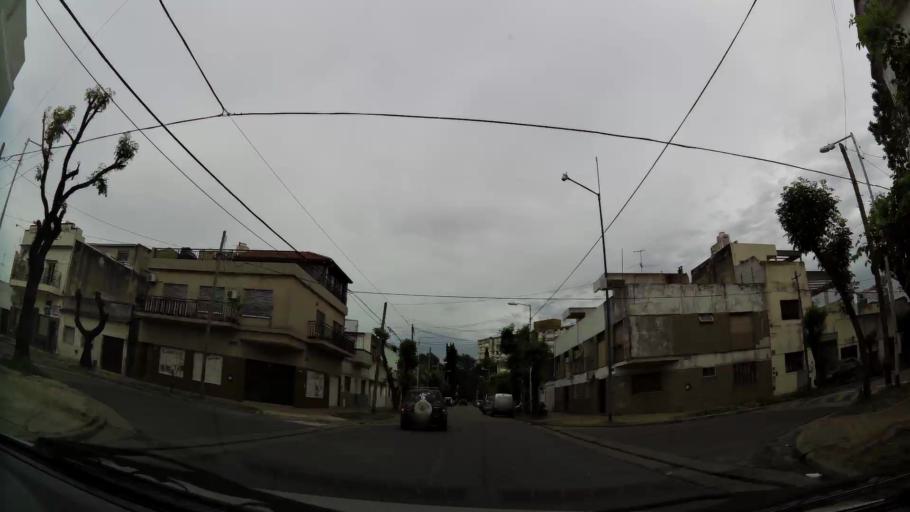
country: AR
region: Buenos Aires
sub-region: Partido de Avellaneda
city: Avellaneda
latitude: -34.6660
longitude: -58.3708
